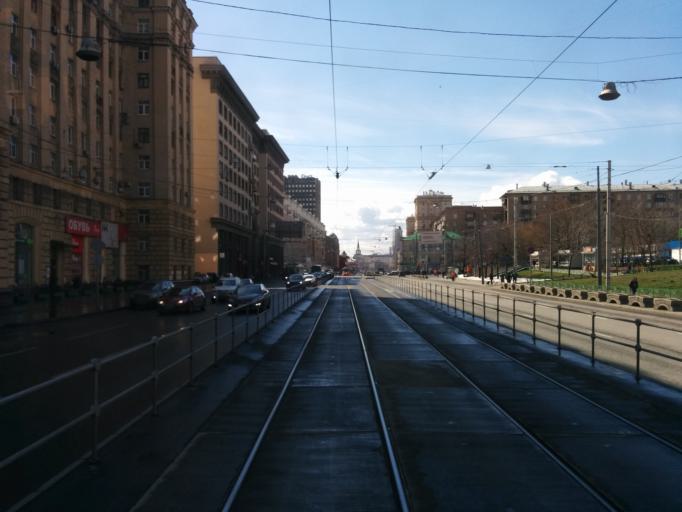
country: RU
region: Moscow
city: Sokol'niki
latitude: 55.7806
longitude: 37.6686
